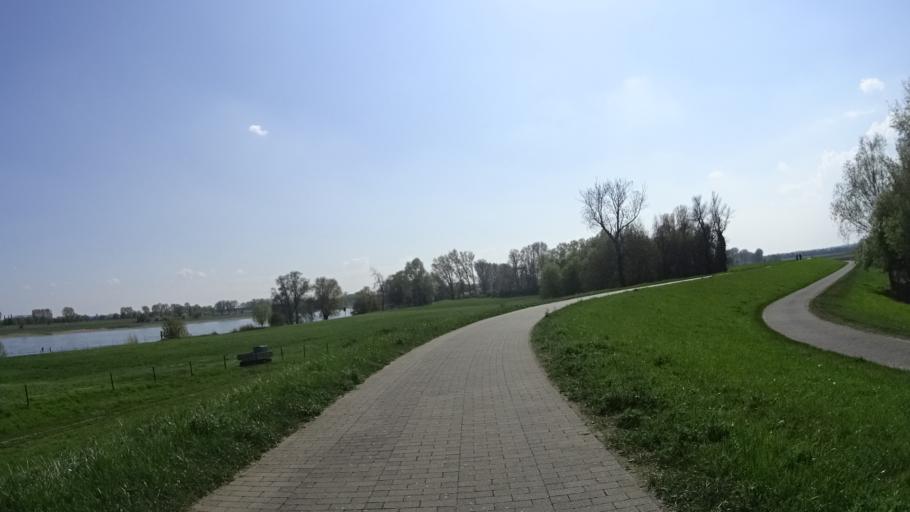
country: DE
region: North Rhine-Westphalia
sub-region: Regierungsbezirk Dusseldorf
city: Meerbusch
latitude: 51.2891
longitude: 6.7106
